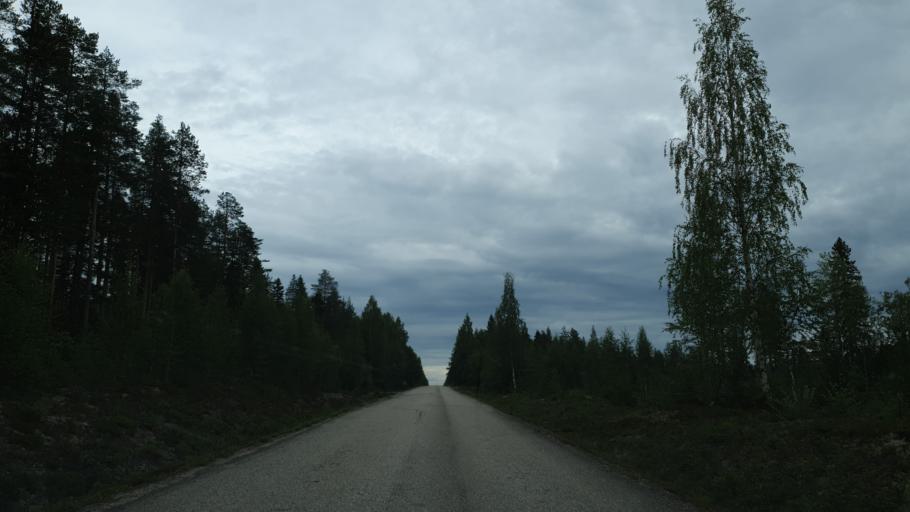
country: FI
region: Kainuu
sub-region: Kehys-Kainuu
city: Kuhmo
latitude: 64.3515
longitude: 29.1137
